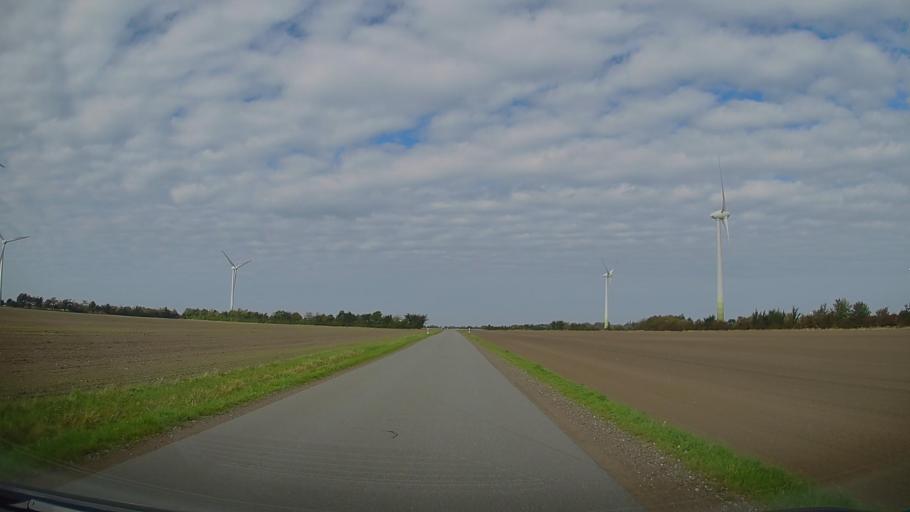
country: DE
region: Schleswig-Holstein
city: Grossenbrode
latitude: 54.5086
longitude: 11.0566
